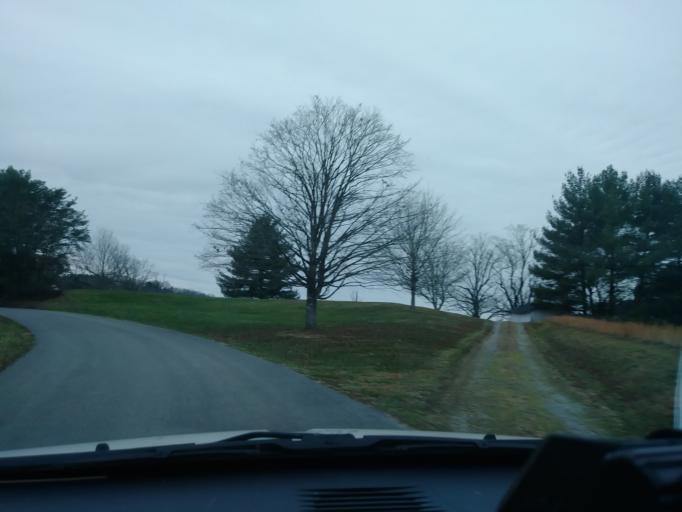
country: US
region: Tennessee
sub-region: Greene County
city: Greeneville
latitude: 36.0810
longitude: -82.8902
